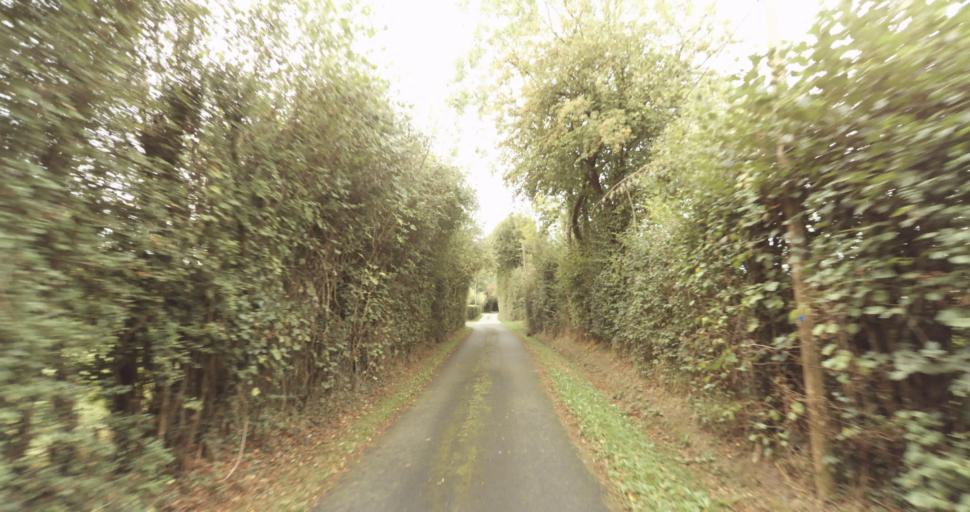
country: FR
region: Lower Normandy
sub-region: Departement de l'Orne
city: Gace
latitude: 48.7507
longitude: 0.3109
